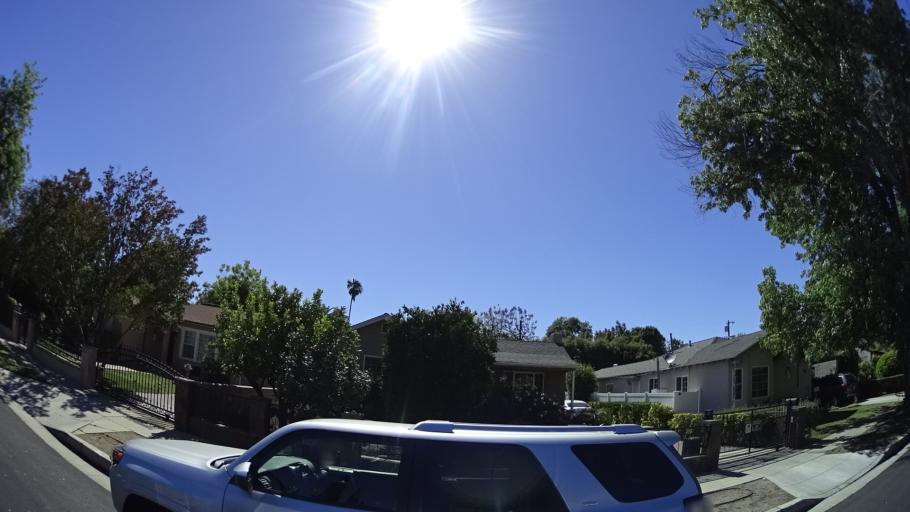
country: US
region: California
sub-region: Los Angeles County
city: Sherman Oaks
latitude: 34.1570
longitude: -118.4585
